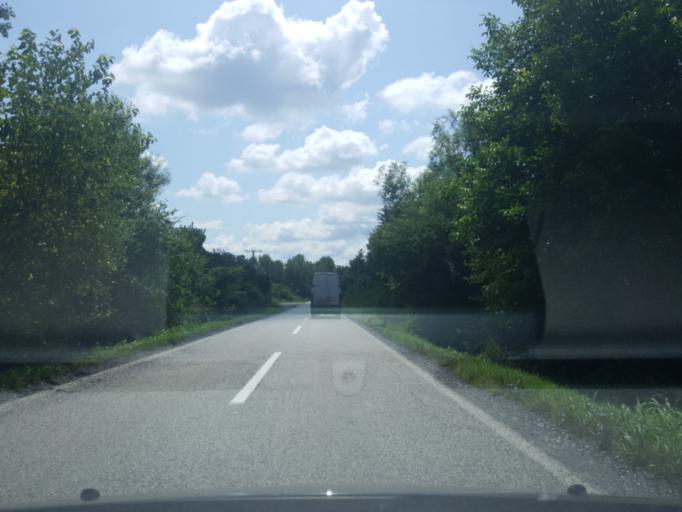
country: RS
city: Glusci
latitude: 44.9068
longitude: 19.5462
